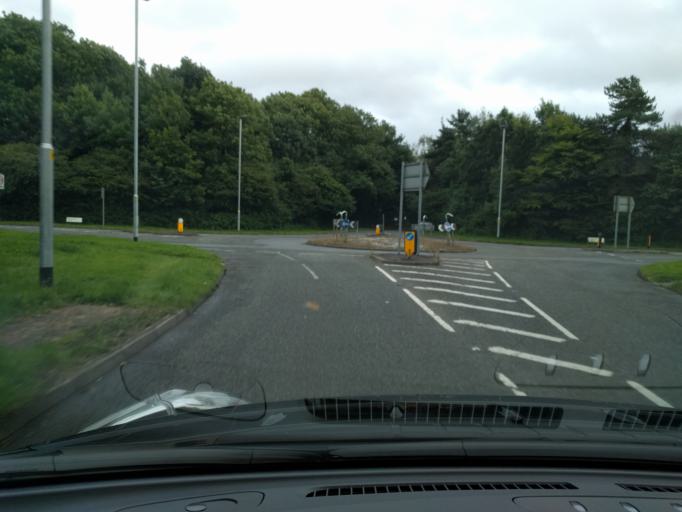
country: GB
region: England
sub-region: Warrington
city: Culcheth
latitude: 53.4255
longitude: -2.5067
